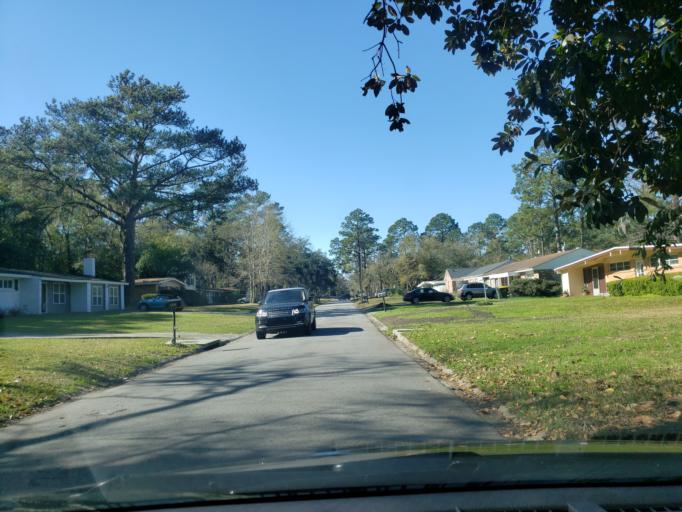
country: US
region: Georgia
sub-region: Chatham County
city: Montgomery
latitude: 31.9708
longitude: -81.1412
